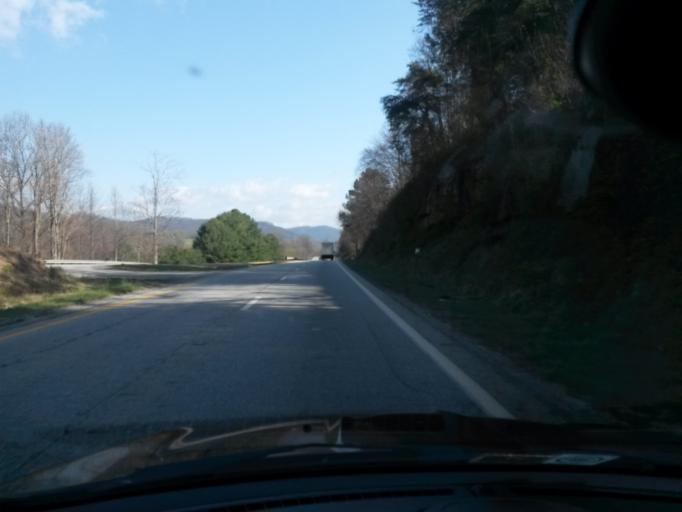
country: US
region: Virginia
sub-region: Nelson County
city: Lovingston
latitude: 37.7848
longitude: -78.8669
